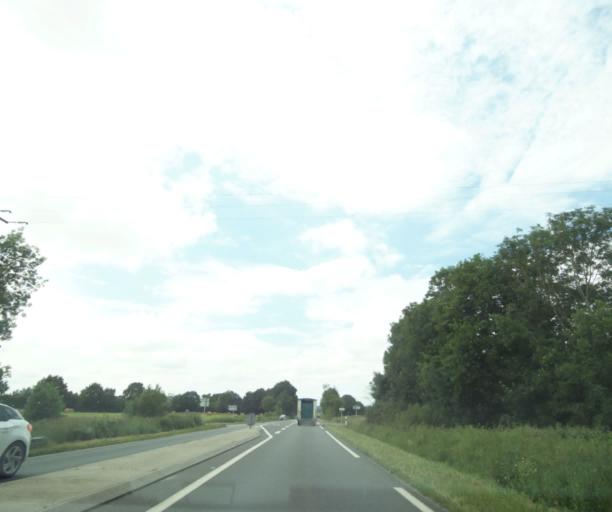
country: FR
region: Poitou-Charentes
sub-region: Departement des Deux-Sevres
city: Champdeniers-Saint-Denis
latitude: 46.4947
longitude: -0.3453
